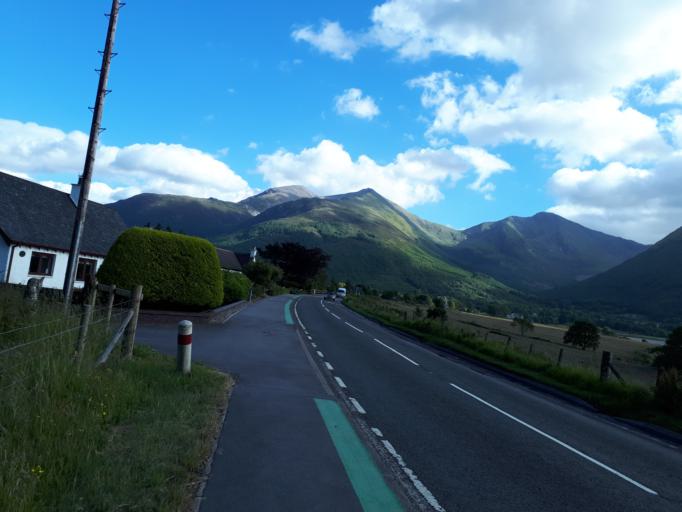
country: GB
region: Scotland
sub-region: Highland
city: Fort William
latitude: 56.6984
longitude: -5.1820
